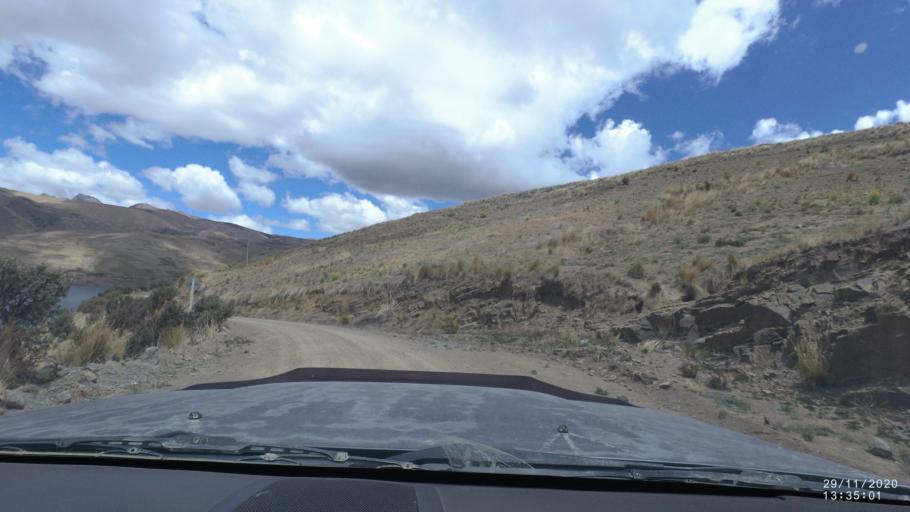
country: BO
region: Cochabamba
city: Cochabamba
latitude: -17.1128
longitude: -66.3341
